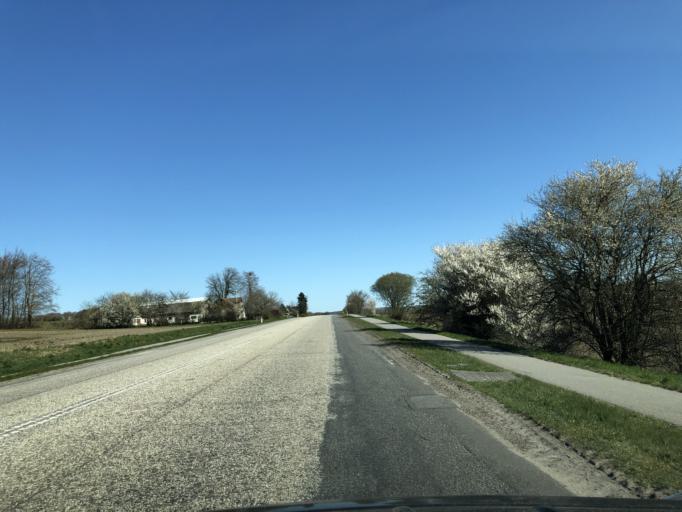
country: DK
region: North Denmark
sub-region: Rebild Kommune
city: Stovring
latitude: 56.9143
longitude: 9.8532
